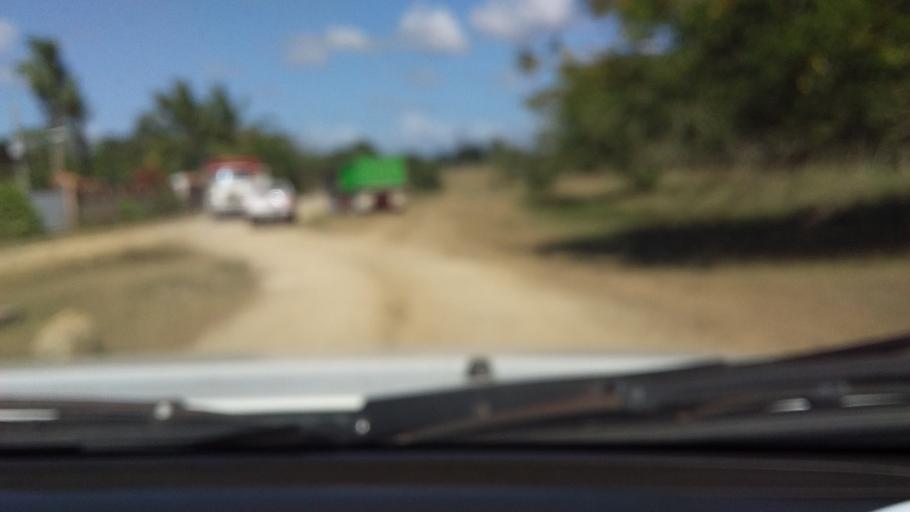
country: DO
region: Santo Domingo
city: Guerra
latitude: 18.5655
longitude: -69.7805
